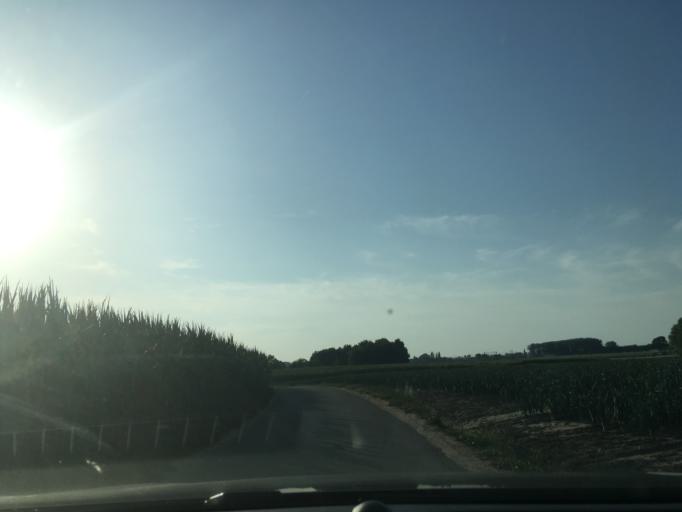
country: BE
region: Flanders
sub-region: Provincie West-Vlaanderen
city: Dentergem
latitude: 50.9856
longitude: 3.3818
